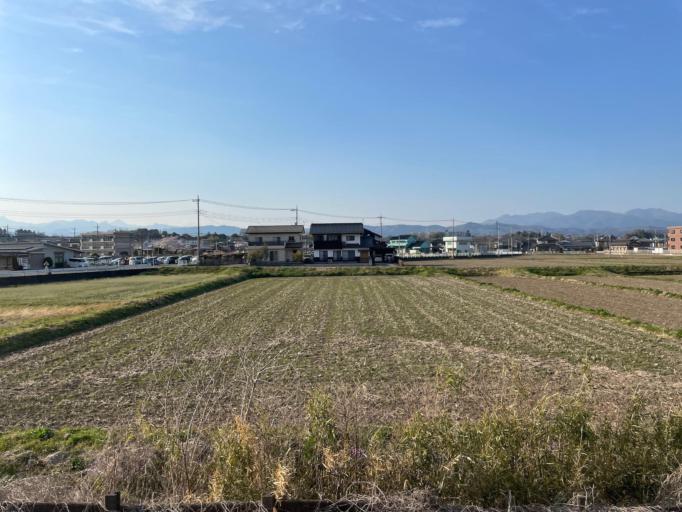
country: JP
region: Gunma
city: Annaka
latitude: 36.2993
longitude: 138.8593
